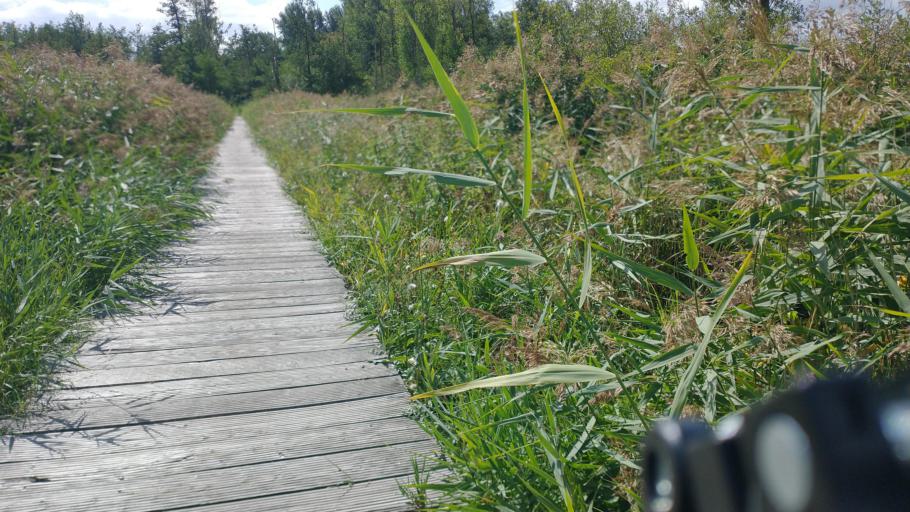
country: DE
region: Schleswig-Holstein
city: Bad Oldesloe
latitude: 53.8181
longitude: 10.3529
